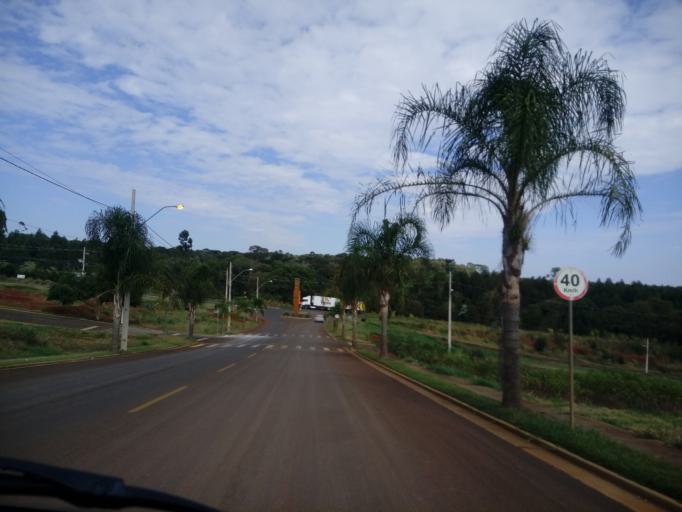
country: BR
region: Santa Catarina
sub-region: Chapeco
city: Chapeco
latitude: -27.0910
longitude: -52.7148
